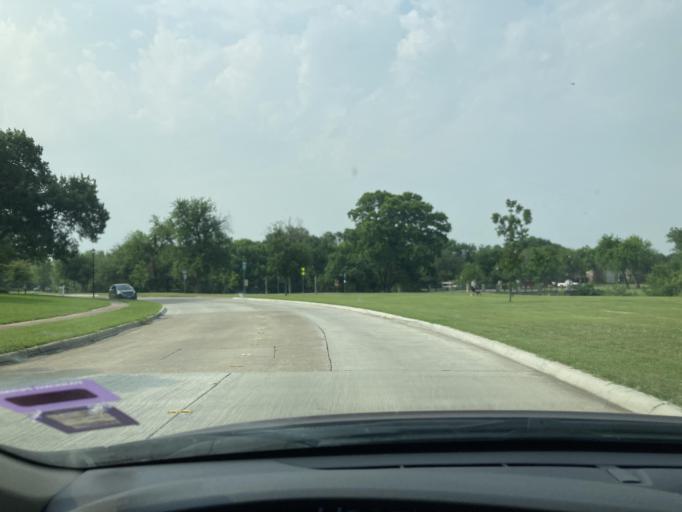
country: US
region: Texas
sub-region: Collin County
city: Plano
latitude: 33.0551
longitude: -96.7292
